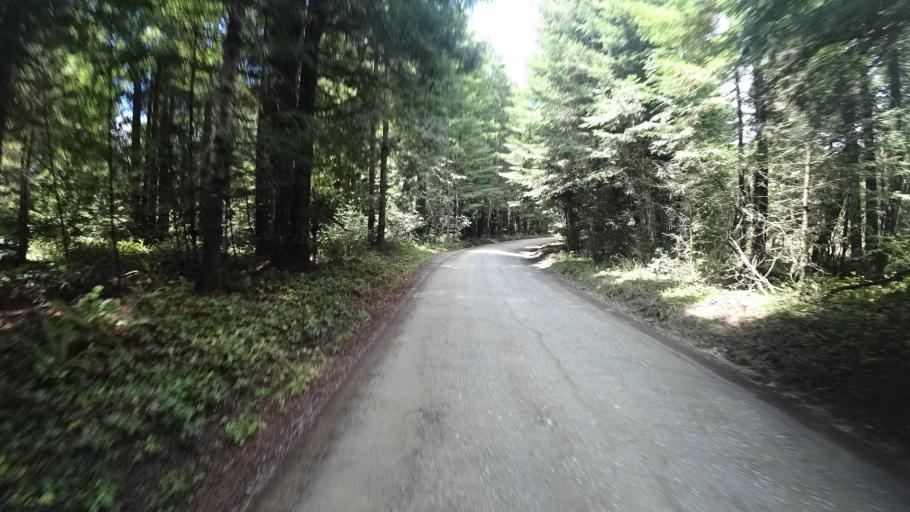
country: US
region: California
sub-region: Humboldt County
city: Blue Lake
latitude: 40.8042
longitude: -123.8820
